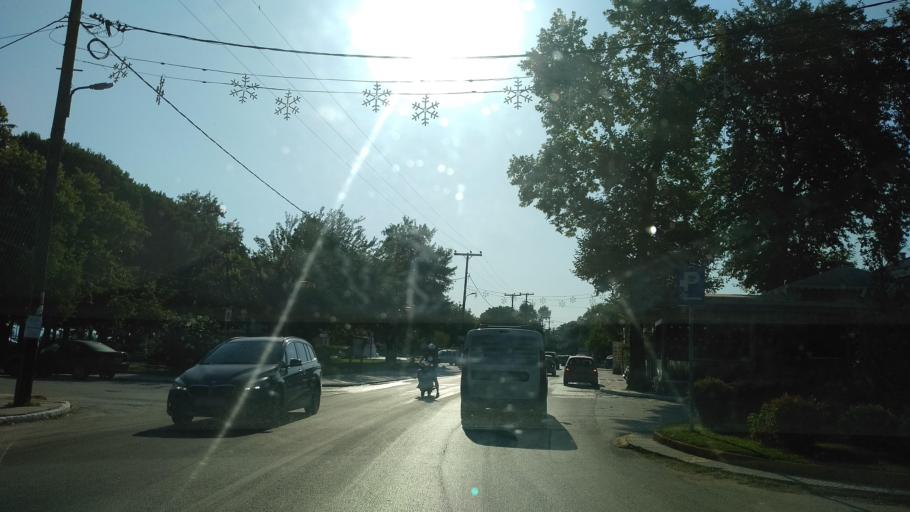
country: GR
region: Central Macedonia
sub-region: Nomos Thessalonikis
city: Stavros
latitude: 40.6652
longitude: 23.6984
